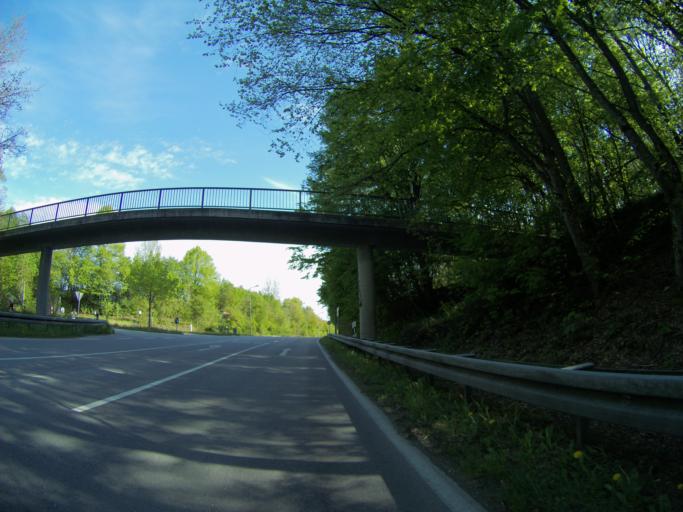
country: DE
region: Bavaria
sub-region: Upper Bavaria
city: Freising
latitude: 48.4064
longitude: 11.7168
